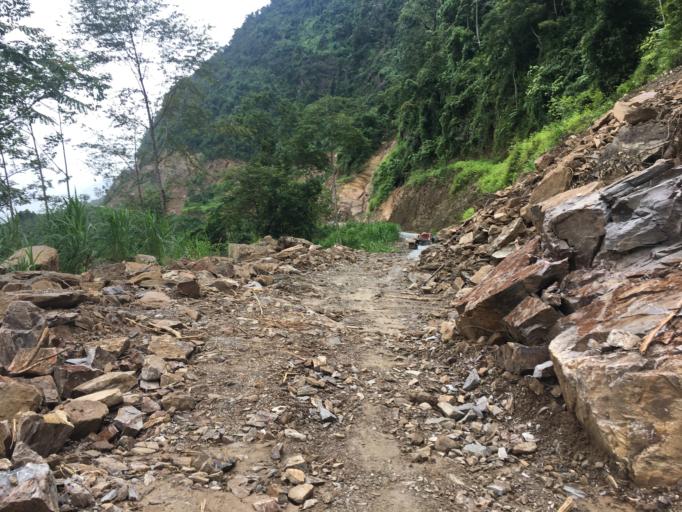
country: VN
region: Ha Giang
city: Thi Tran Tam Son
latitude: 22.9807
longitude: 105.0605
